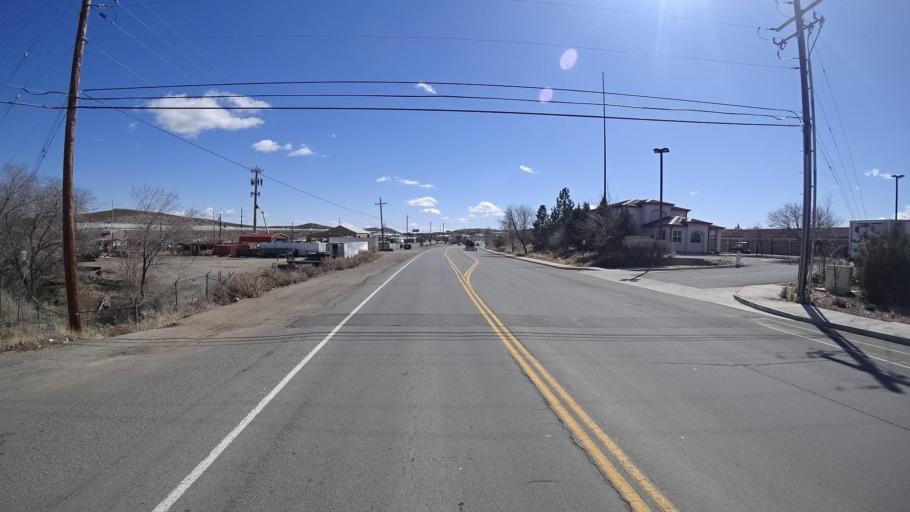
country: US
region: Nevada
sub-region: Washoe County
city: Golden Valley
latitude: 39.5991
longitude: -119.8415
